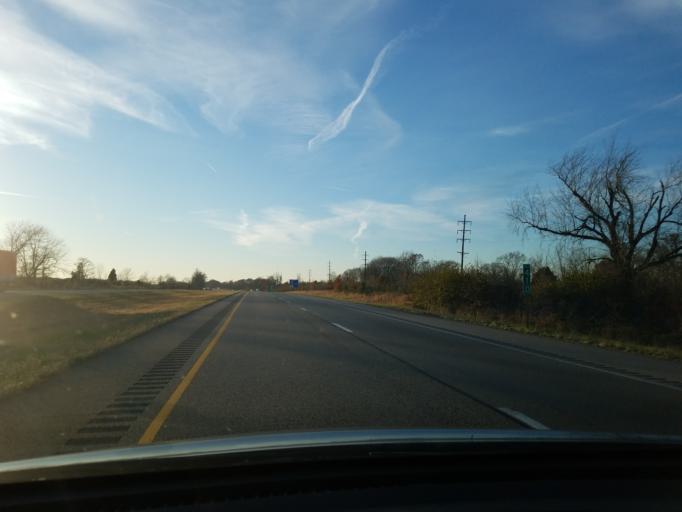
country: US
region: Indiana
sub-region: Warrick County
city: Boonville
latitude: 38.1996
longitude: -87.2644
